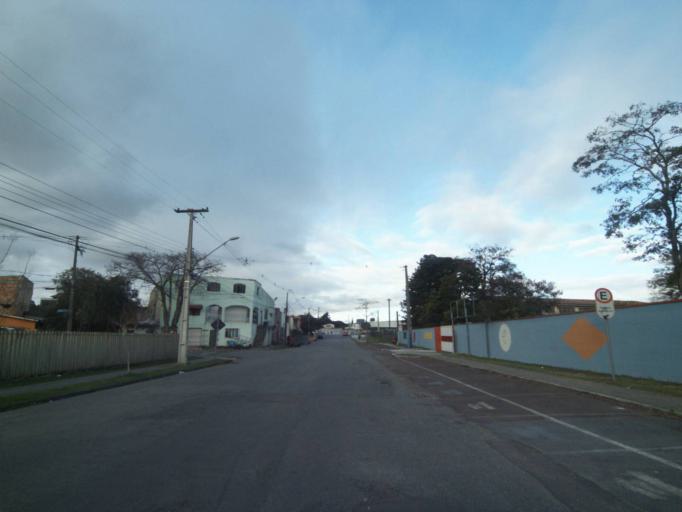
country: BR
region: Parana
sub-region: Curitiba
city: Curitiba
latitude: -25.4502
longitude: -49.2470
